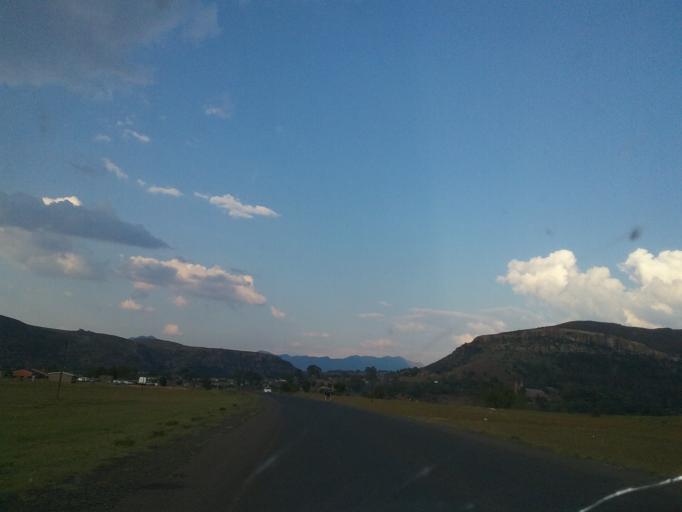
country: LS
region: Quthing
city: Quthing
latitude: -30.3982
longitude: 27.6557
